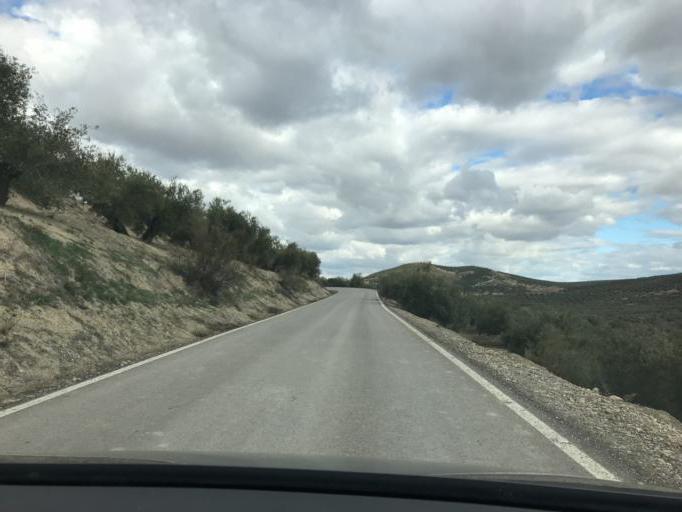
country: ES
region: Andalusia
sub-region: Provincia de Jaen
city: Jimena
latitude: 37.8822
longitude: -3.4690
